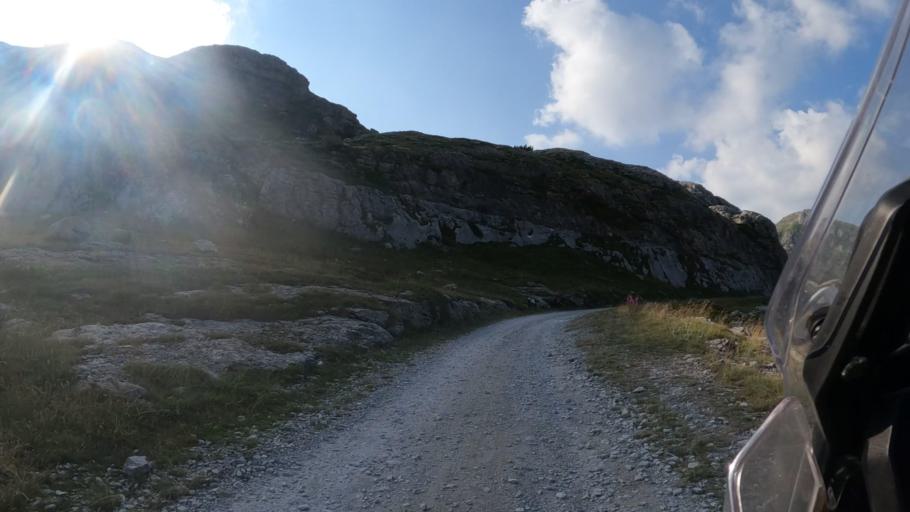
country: IT
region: Piedmont
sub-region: Provincia di Cuneo
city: Limone Piemonte
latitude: 44.1629
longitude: 7.6696
